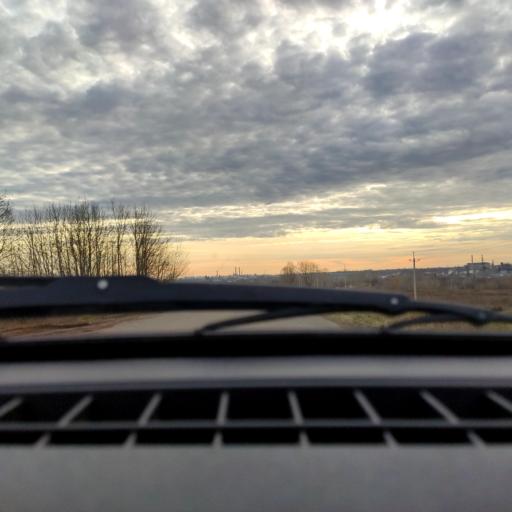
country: RU
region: Bashkortostan
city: Blagoveshchensk
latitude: 54.8905
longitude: 56.1465
